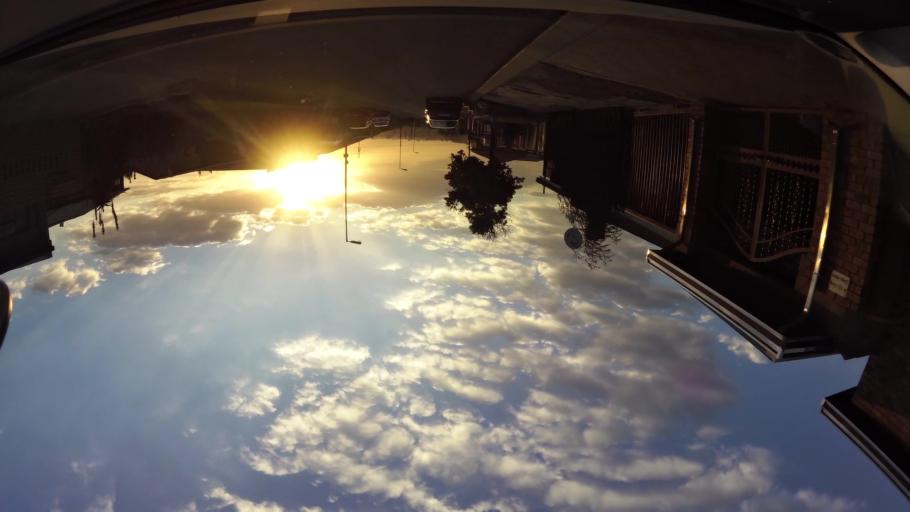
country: ZA
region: Gauteng
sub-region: City of Johannesburg Metropolitan Municipality
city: Soweto
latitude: -26.2718
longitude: 27.8932
